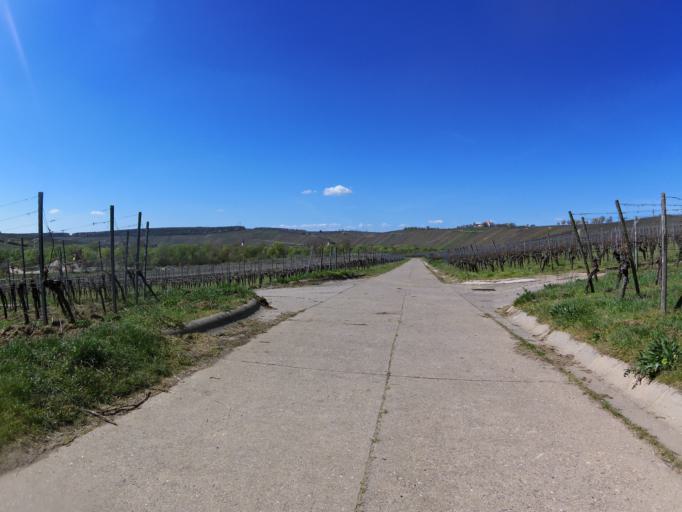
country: DE
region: Bavaria
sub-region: Regierungsbezirk Unterfranken
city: Nordheim
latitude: 49.8620
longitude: 10.2052
